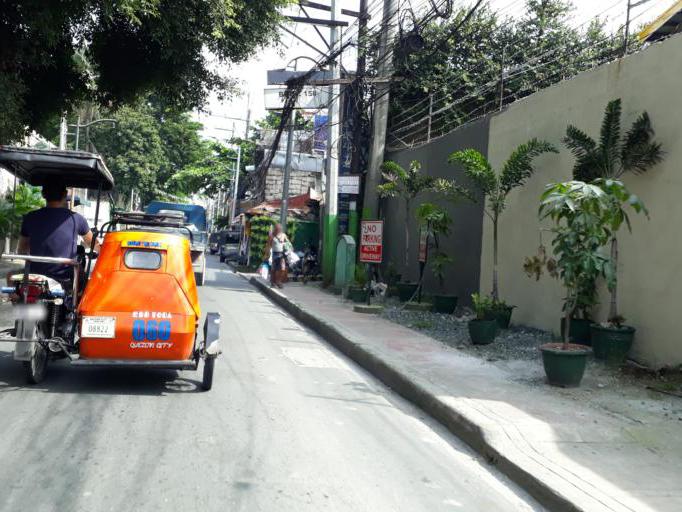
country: PH
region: Calabarzon
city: Bagong Pagasa
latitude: 14.6708
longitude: 121.0060
